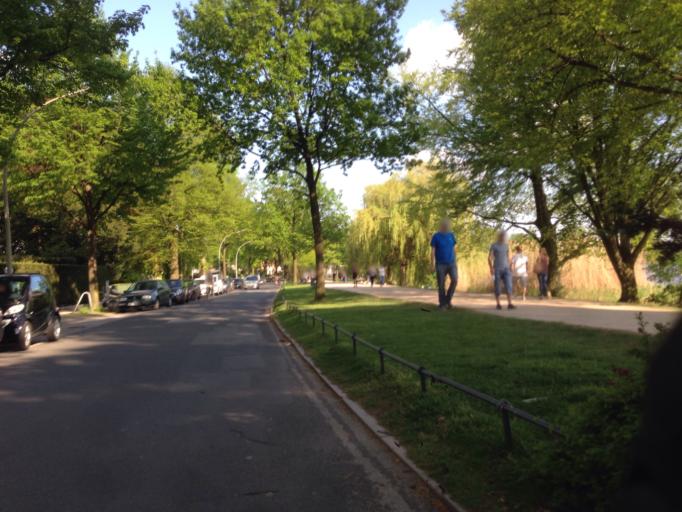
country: DE
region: Hamburg
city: Hamburg
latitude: 53.5693
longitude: 10.0125
